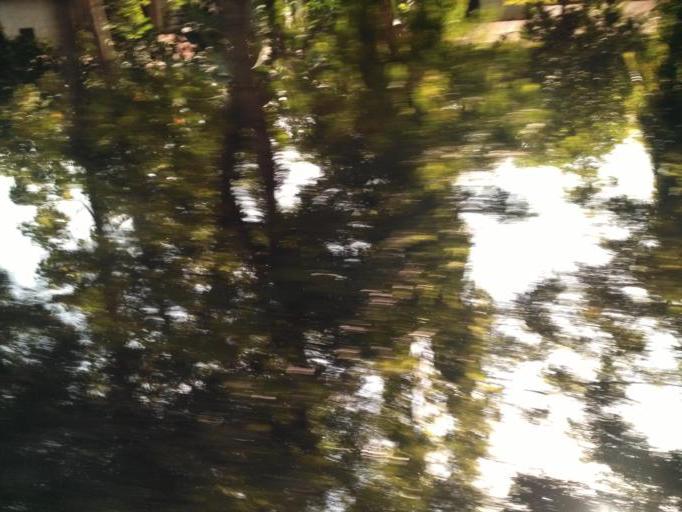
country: TZ
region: Mwanza
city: Mwanza
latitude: -2.4983
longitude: 32.8975
